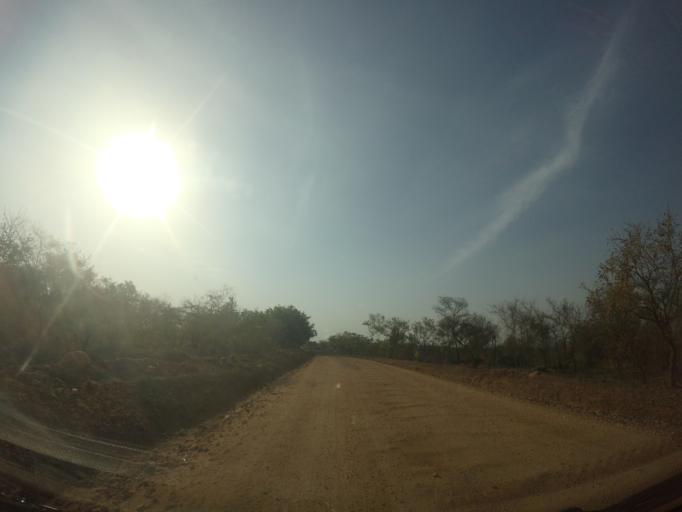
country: UG
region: Northern Region
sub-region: Maracha District
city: Maracha
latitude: 3.1130
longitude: 31.1389
